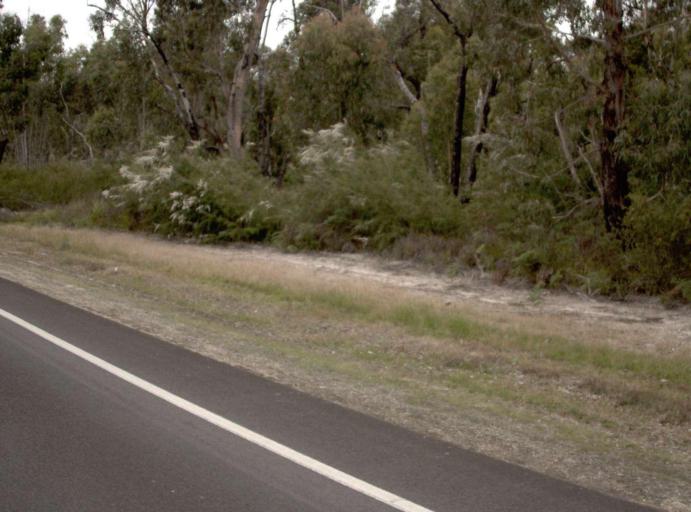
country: AU
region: Victoria
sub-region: Wellington
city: Sale
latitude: -38.3203
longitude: 147.0224
